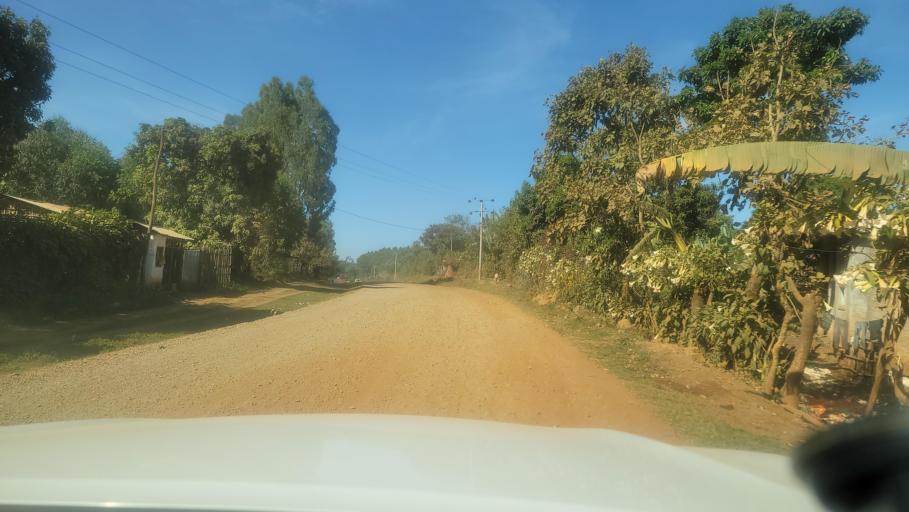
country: ET
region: Oromiya
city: Agaro
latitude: 7.7975
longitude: 36.4882
